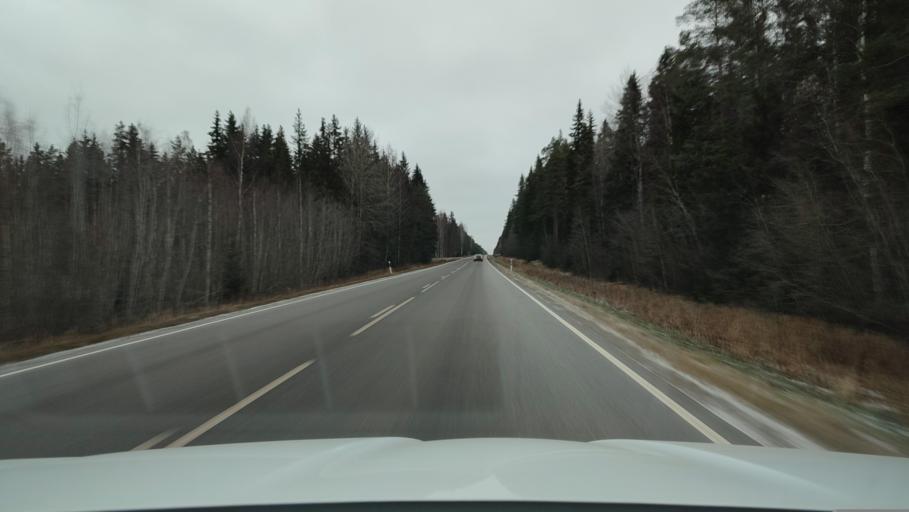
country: FI
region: Ostrobothnia
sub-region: Sydosterbotten
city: Naerpes
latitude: 62.5496
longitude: 21.4719
